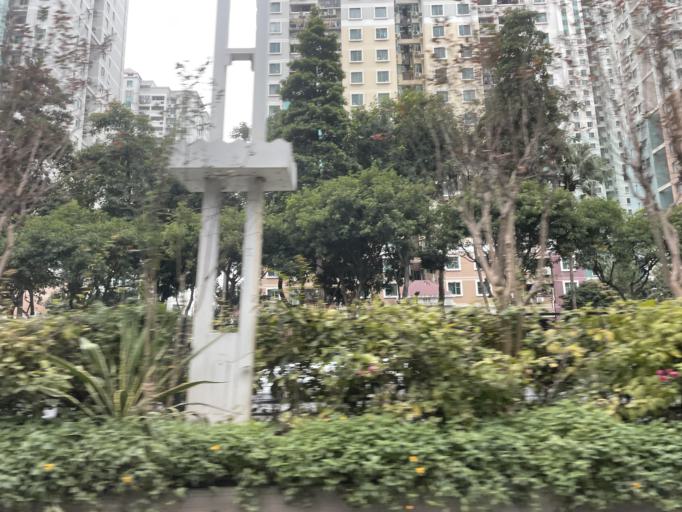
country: CN
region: Guangdong
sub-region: Shenzhen
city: Shenzhen
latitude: 22.5198
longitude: 114.0446
